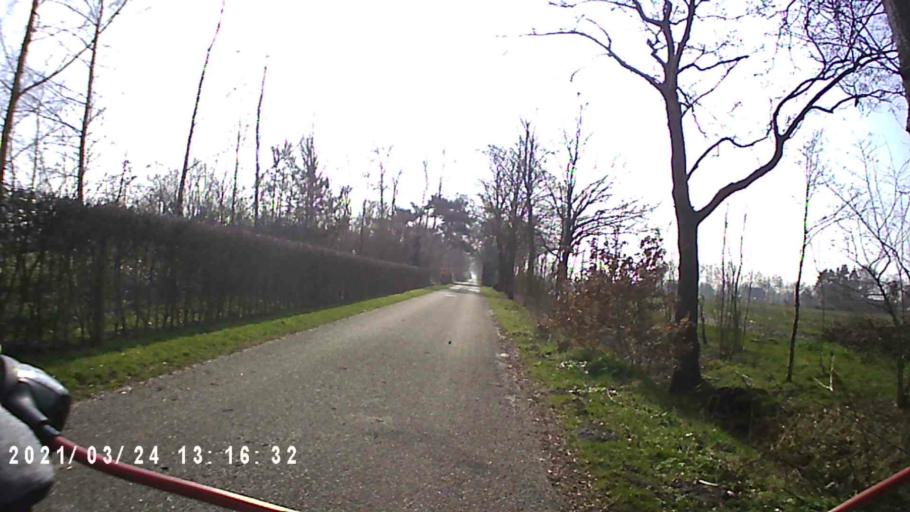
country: NL
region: Groningen
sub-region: Gemeente Leek
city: Leek
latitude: 53.1123
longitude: 6.2911
